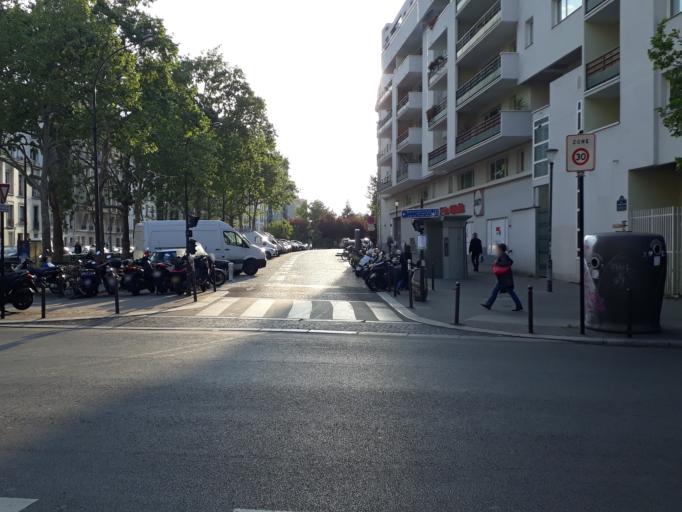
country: FR
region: Ile-de-France
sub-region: Paris
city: Saint-Ouen
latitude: 48.8958
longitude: 2.3285
